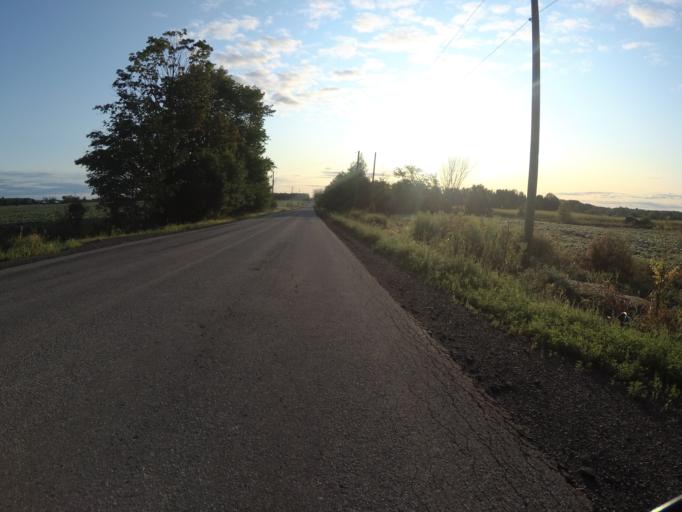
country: CA
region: Ontario
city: Casselman
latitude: 45.1558
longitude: -75.4159
